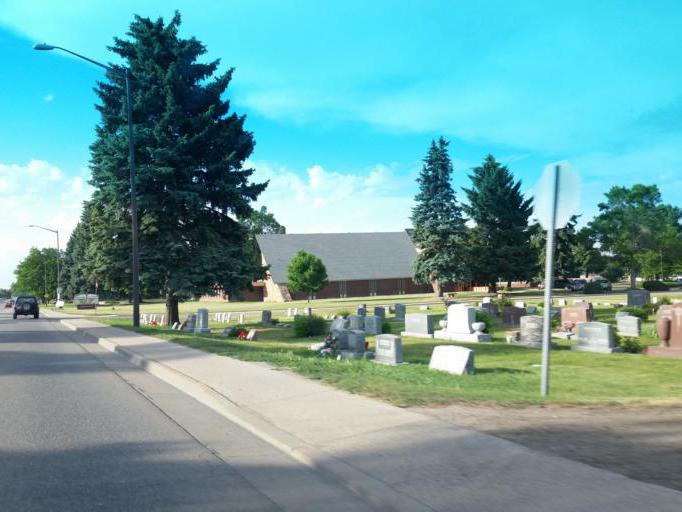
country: US
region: Colorado
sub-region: Larimer County
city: Loveland
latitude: 40.4122
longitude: -105.0730
